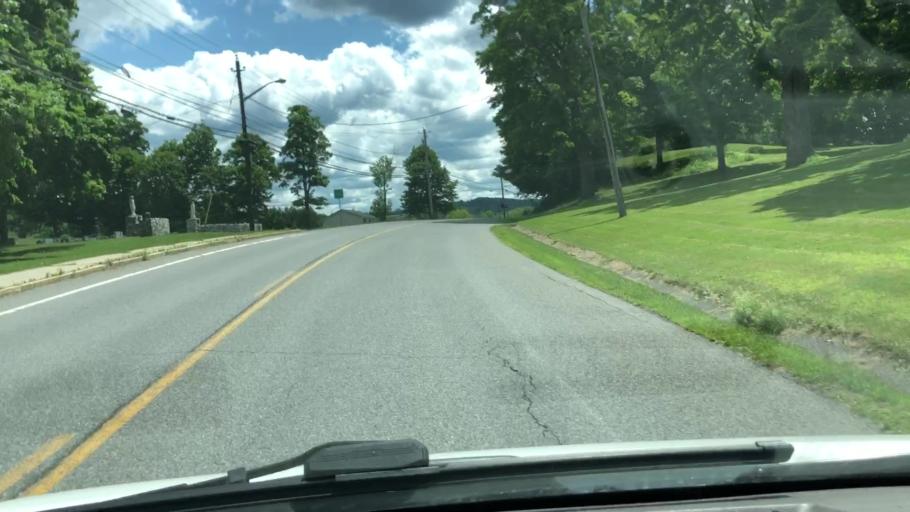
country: US
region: Massachusetts
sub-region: Berkshire County
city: Adams
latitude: 42.6018
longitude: -73.1172
